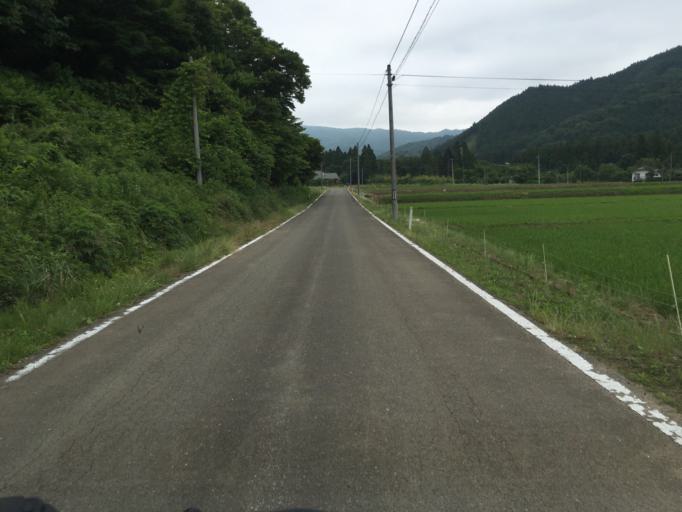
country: JP
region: Miyagi
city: Marumori
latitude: 37.7692
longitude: 140.8409
